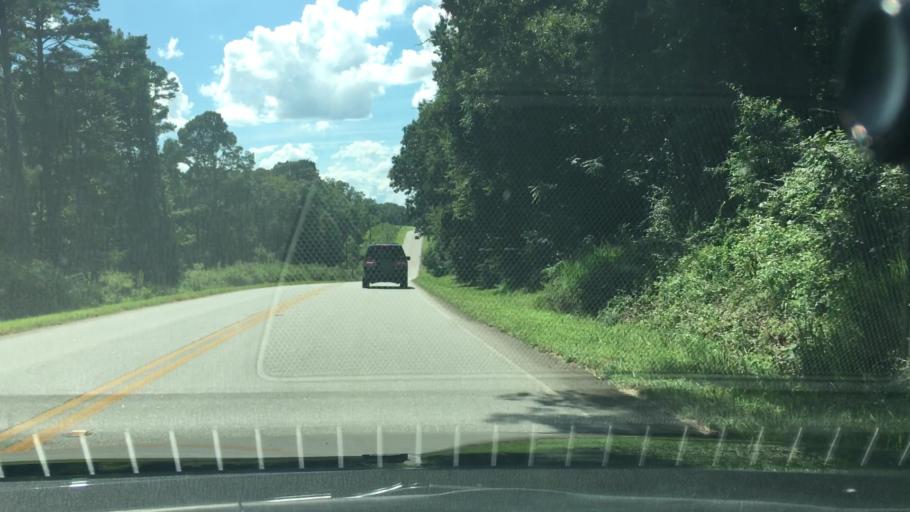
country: US
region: Georgia
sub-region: Jasper County
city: Monticello
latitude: 33.3049
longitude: -83.5768
